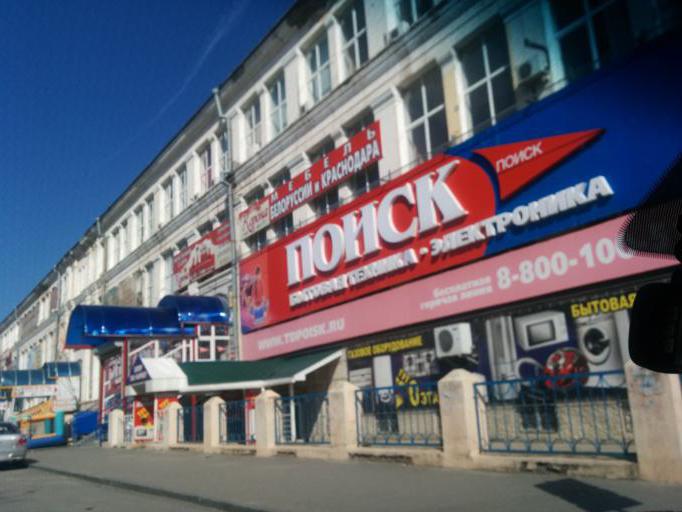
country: RU
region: Rostov
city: Shakhty
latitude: 47.6998
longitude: 40.2095
